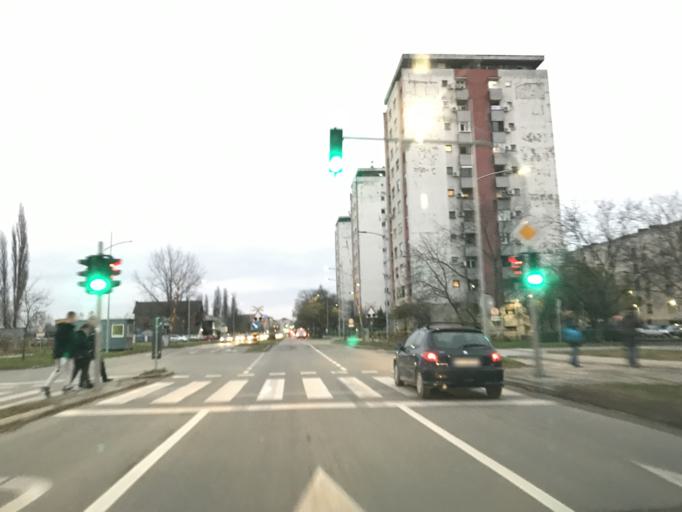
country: RS
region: Autonomna Pokrajina Vojvodina
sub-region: Juznobacki Okrug
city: Novi Sad
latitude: 45.2678
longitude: 19.8121
